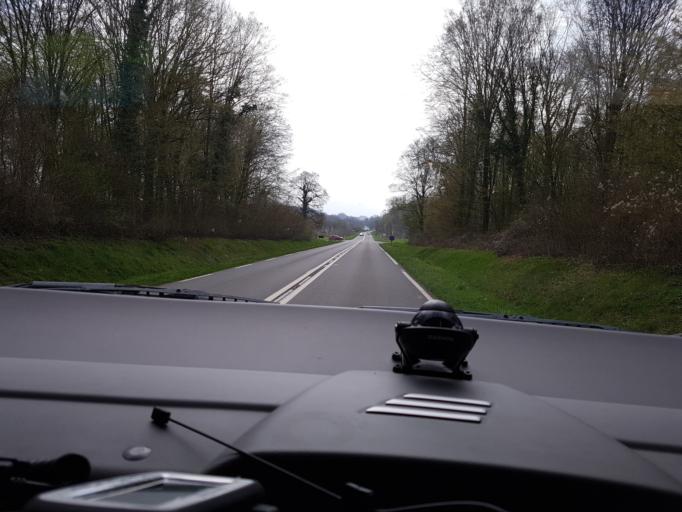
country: FR
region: Picardie
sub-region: Departement de l'Aisne
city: Coucy-le-Chateau-Auffrique
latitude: 49.5010
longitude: 3.3297
